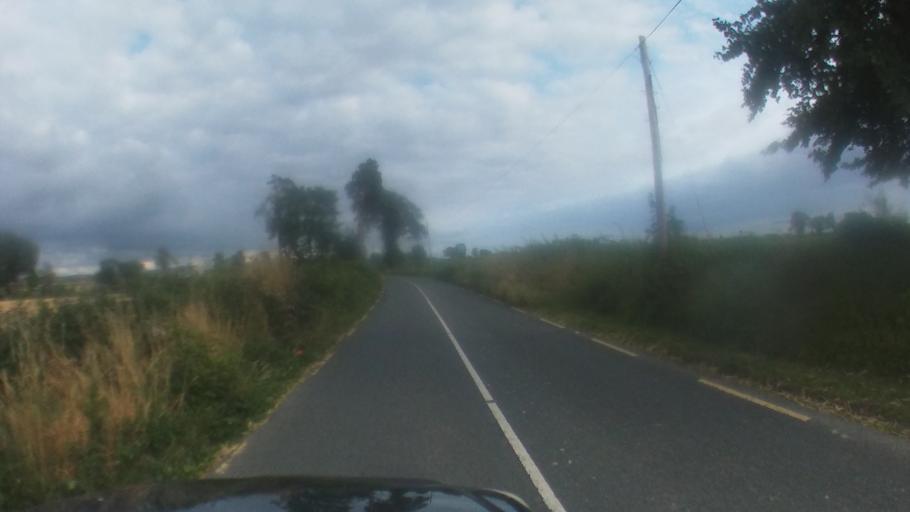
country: IE
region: Leinster
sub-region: Kildare
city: Athy
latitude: 52.9931
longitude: -6.9837
